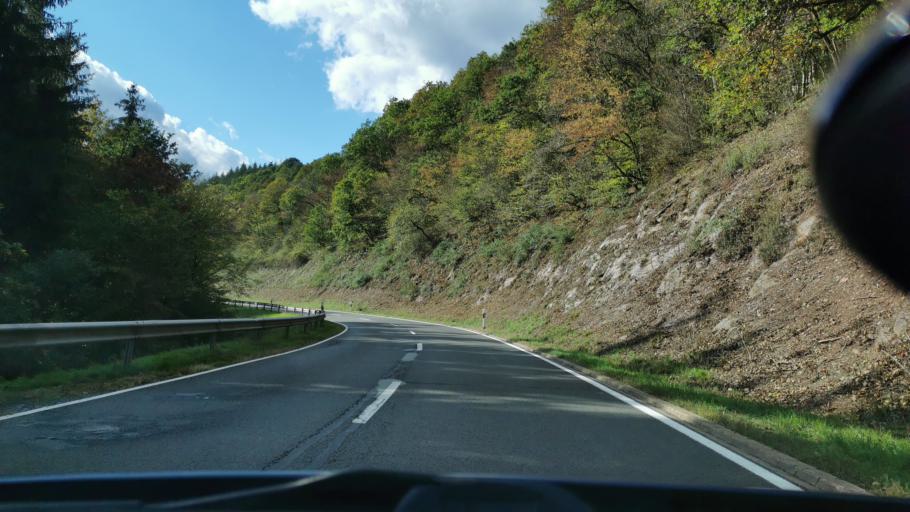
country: DE
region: Rheinland-Pfalz
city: Musweiler
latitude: 50.0010
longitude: 6.8064
